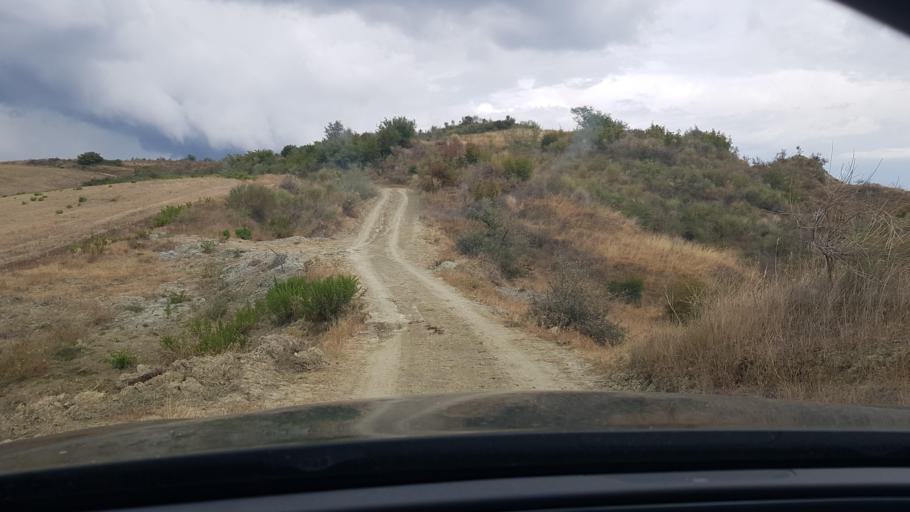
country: AL
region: Durres
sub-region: Rrethi i Durresit
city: Gjepalaj
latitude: 41.2965
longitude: 19.5516
